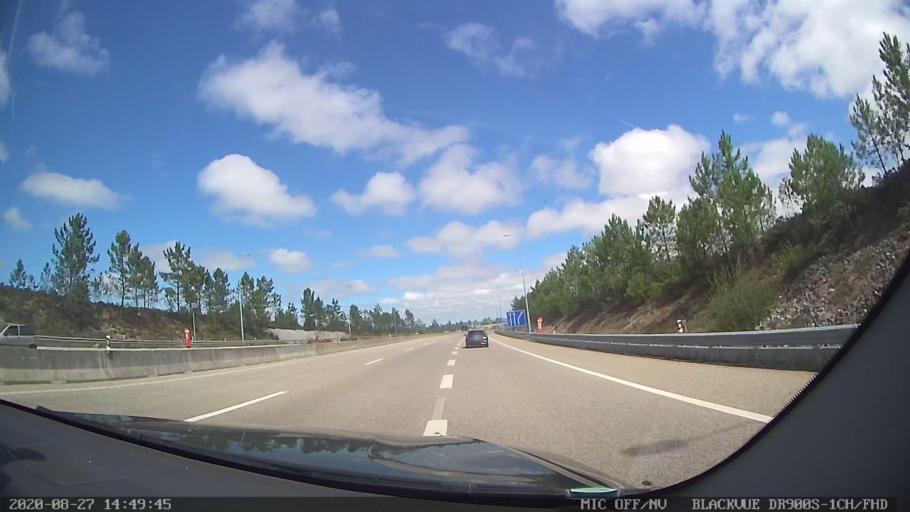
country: PT
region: Leiria
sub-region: Marinha Grande
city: Marinha Grande
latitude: 39.7413
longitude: -8.8790
